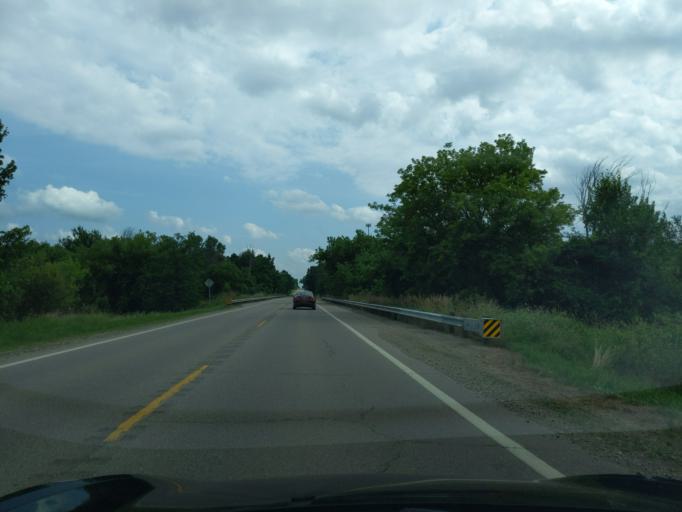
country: US
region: Michigan
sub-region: Eaton County
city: Eaton Rapids
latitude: 42.4450
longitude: -84.6497
